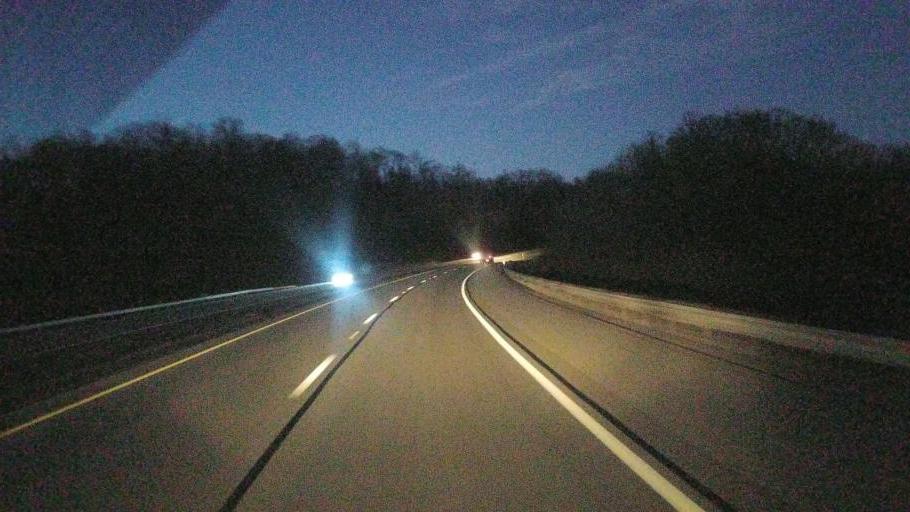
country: US
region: West Virginia
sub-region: Wood County
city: Mineral Wells
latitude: 39.2212
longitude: -81.5276
